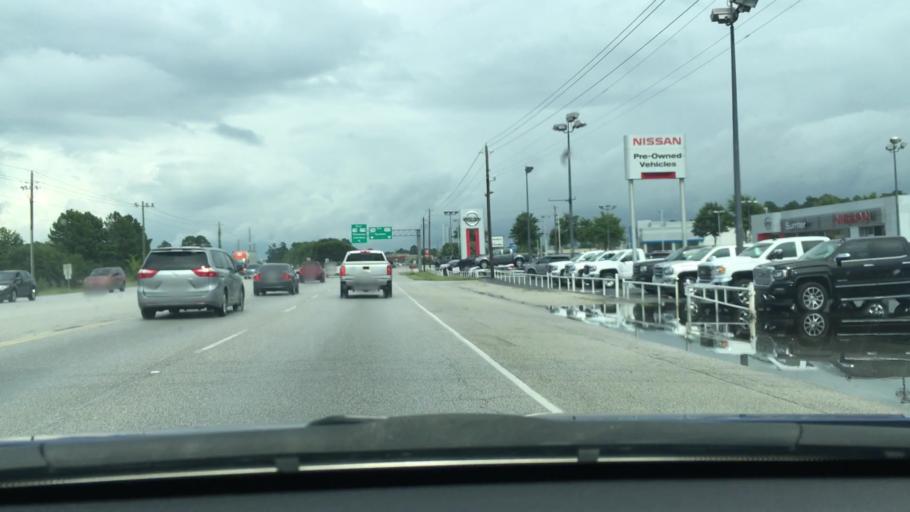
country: US
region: South Carolina
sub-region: Sumter County
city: Sumter
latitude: 33.9567
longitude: -80.3868
